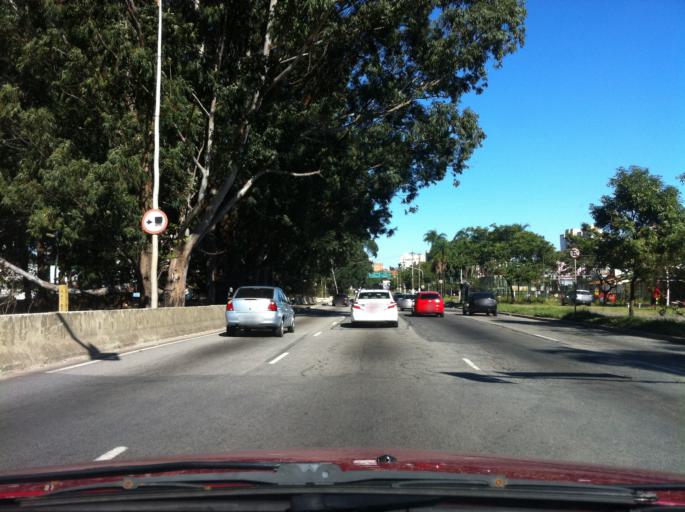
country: BR
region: Sao Paulo
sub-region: Ferraz De Vasconcelos
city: Ferraz de Vasconcelos
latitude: -23.5278
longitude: -46.4578
